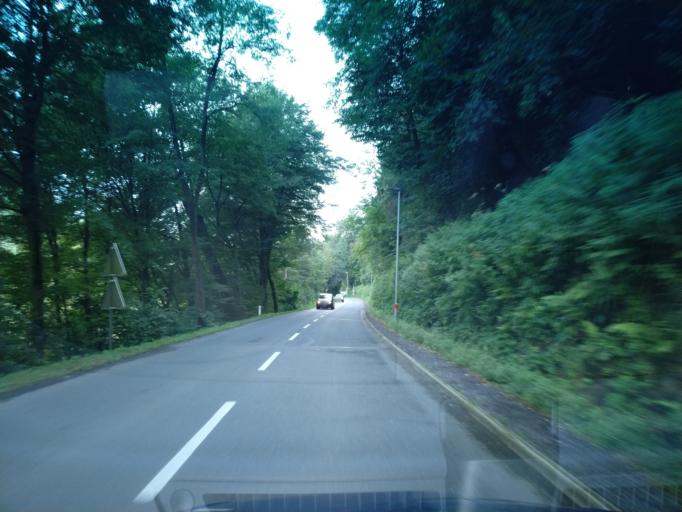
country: AT
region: Styria
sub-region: Politischer Bezirk Leibnitz
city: Leibnitz
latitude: 46.7818
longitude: 15.5262
